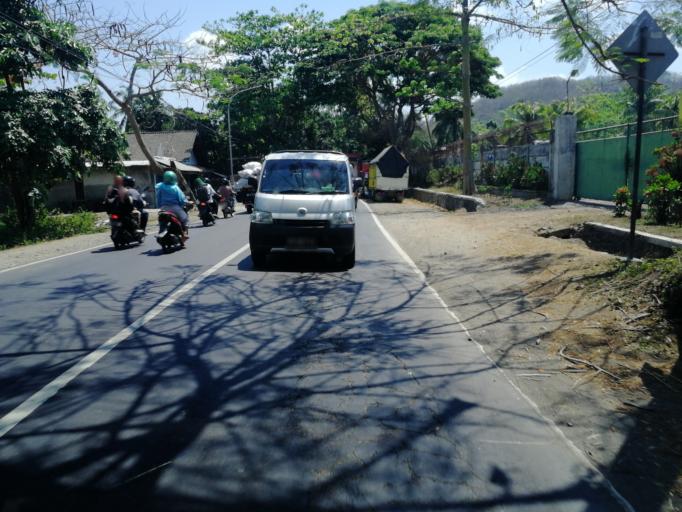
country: ID
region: West Nusa Tenggara
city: Jelateng Timur
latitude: -8.6966
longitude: 116.1062
